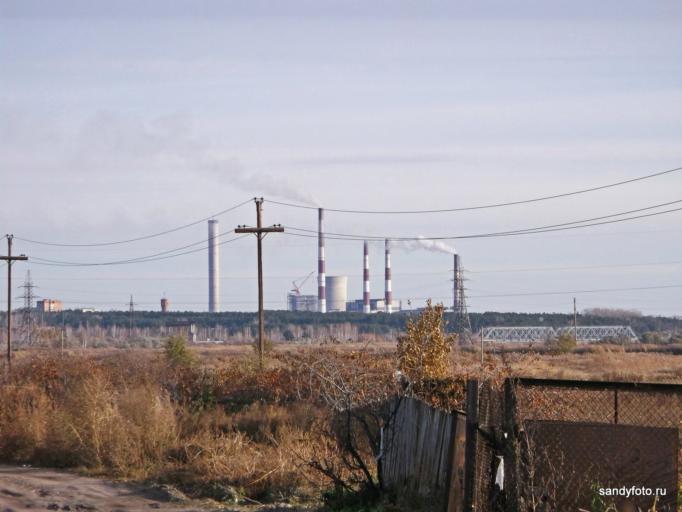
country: RU
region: Chelyabinsk
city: Troitsk
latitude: 54.0731
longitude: 61.5824
